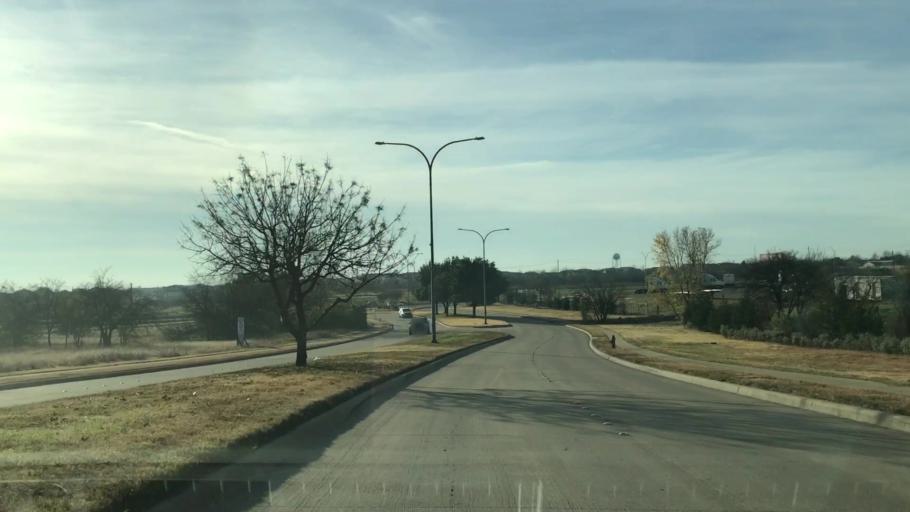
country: US
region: Texas
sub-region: Tarrant County
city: Sansom Park
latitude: 32.8202
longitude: -97.4054
